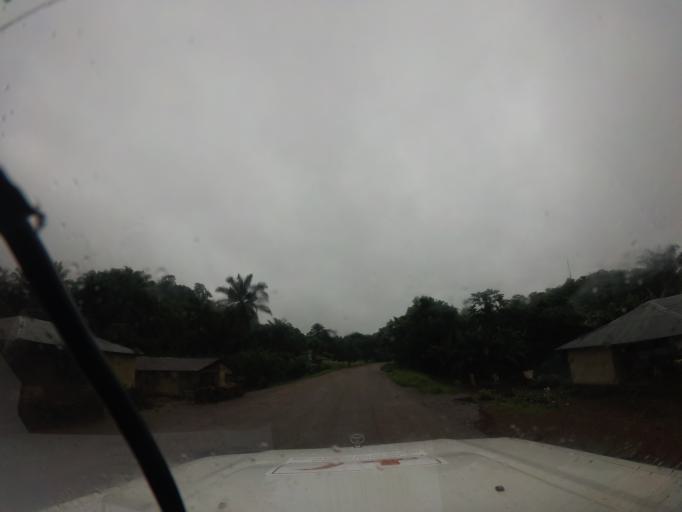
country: SL
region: Northern Province
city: Kabala
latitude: 9.4664
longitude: -11.6779
